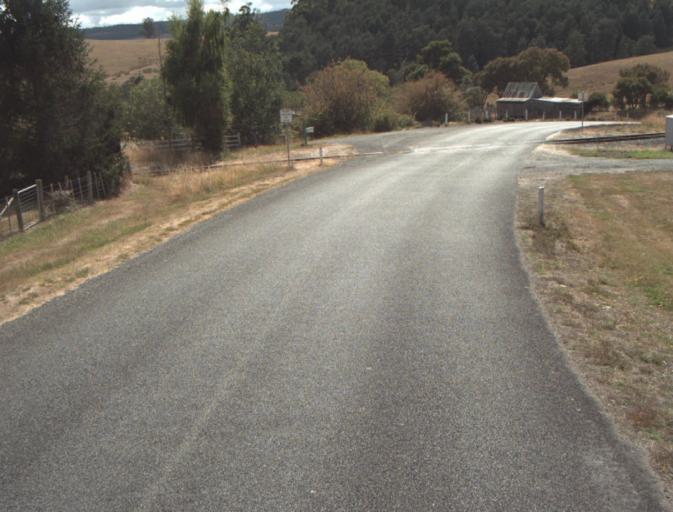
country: AU
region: Tasmania
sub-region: Launceston
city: Mayfield
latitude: -41.2573
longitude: 147.1940
